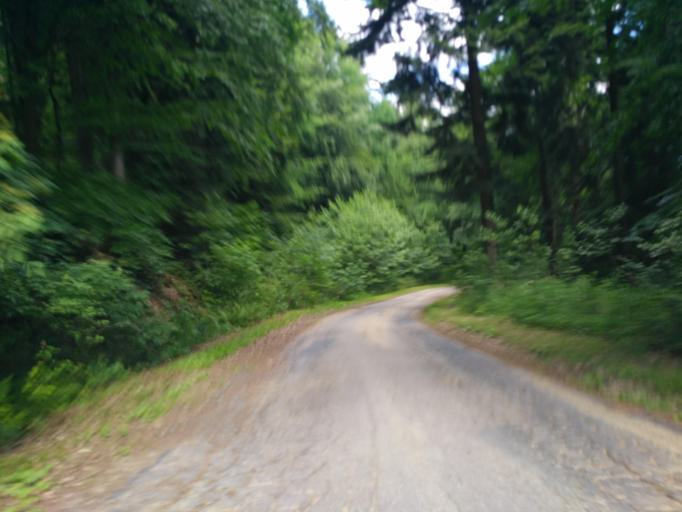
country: PL
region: Subcarpathian Voivodeship
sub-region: Powiat jasielski
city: Brzyska
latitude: 49.8057
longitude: 21.3672
